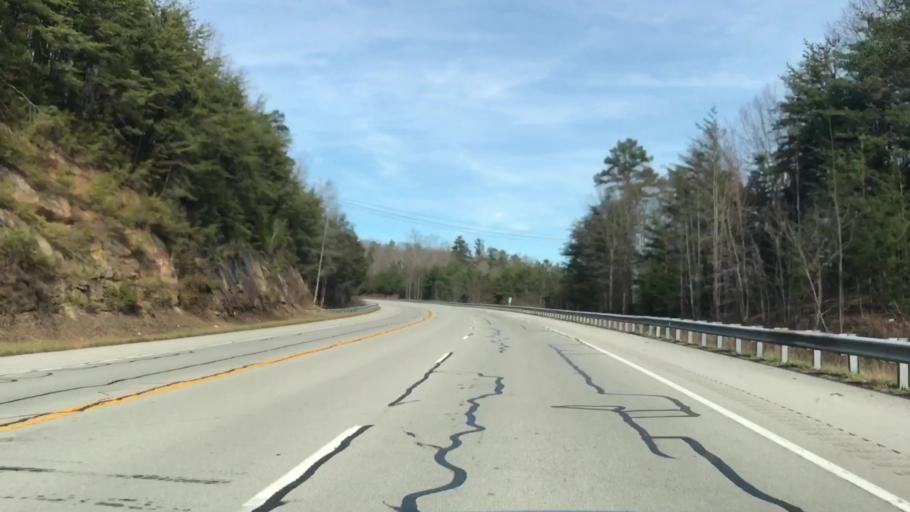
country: US
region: Kentucky
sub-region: McCreary County
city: Whitley City
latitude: 36.8606
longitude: -84.4874
